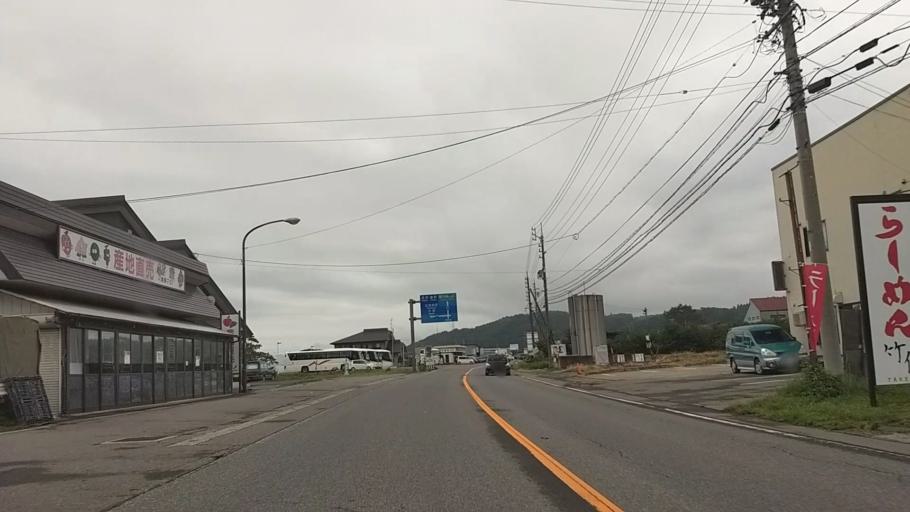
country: JP
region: Nagano
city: Iiyama
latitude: 36.8275
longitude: 138.3540
